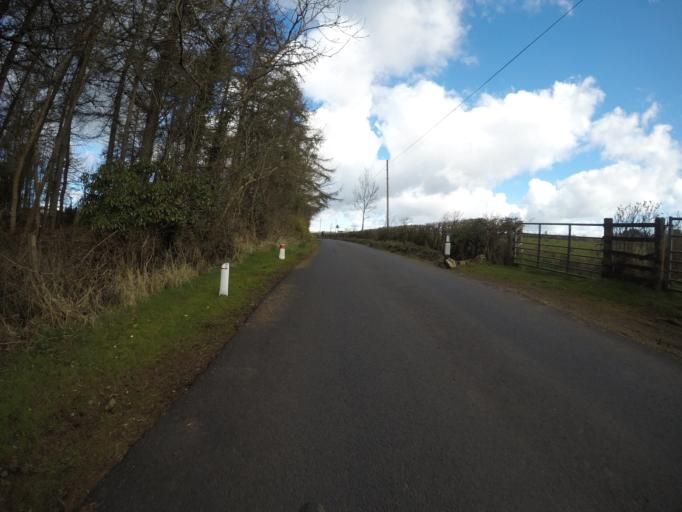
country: GB
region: Scotland
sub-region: North Ayrshire
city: Dalry
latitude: 55.6925
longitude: -4.6740
